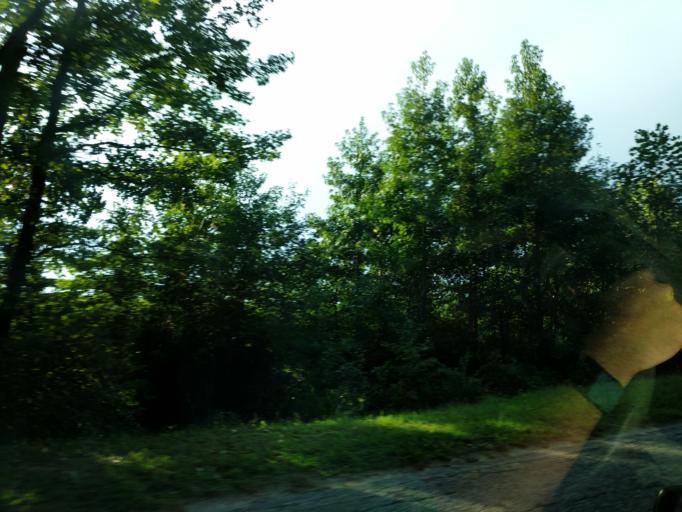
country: US
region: South Carolina
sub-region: Anderson County
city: Piedmont
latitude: 34.6970
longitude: -82.5025
